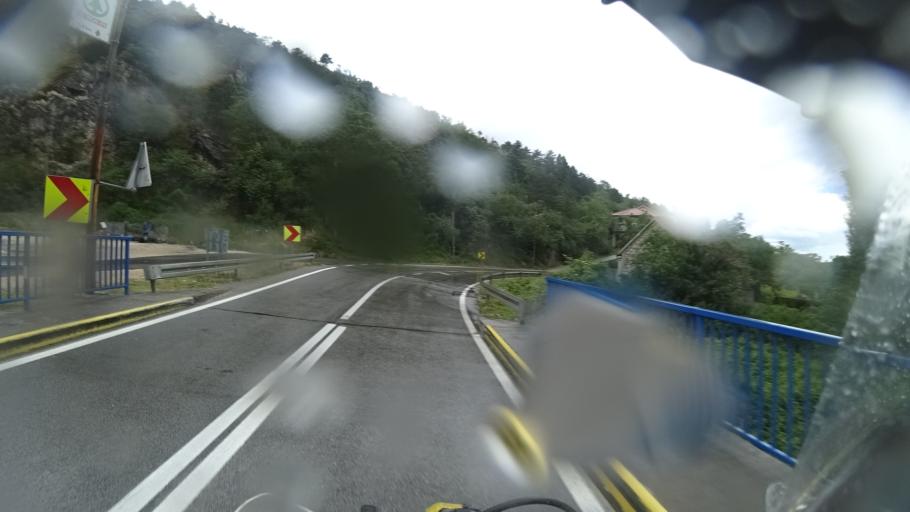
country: HR
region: Sibensko-Kniniska
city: Knin
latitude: 44.0410
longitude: 16.1868
